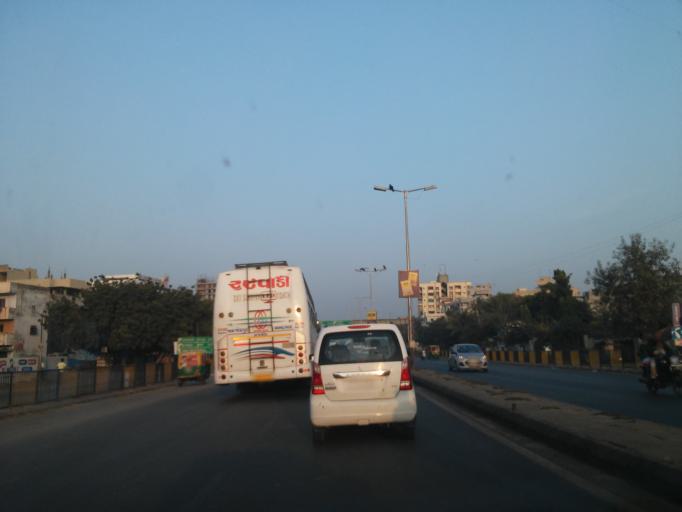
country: IN
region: Gujarat
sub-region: Ahmadabad
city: Sarkhej
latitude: 22.9947
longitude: 72.5300
